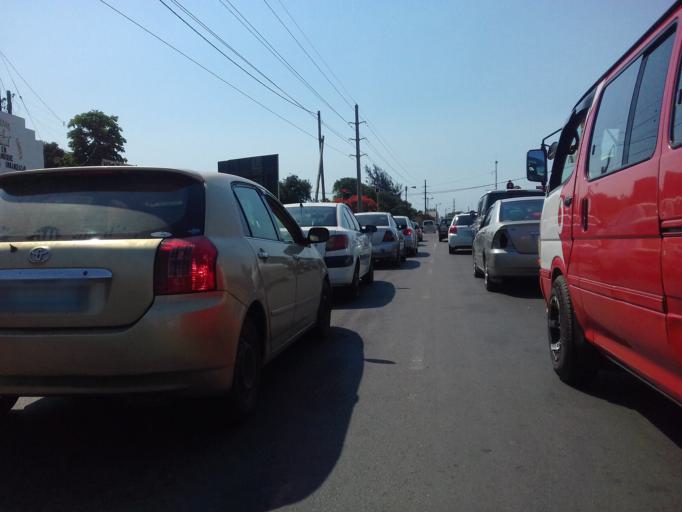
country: MZ
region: Maputo City
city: Maputo
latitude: -25.9442
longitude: 32.5737
